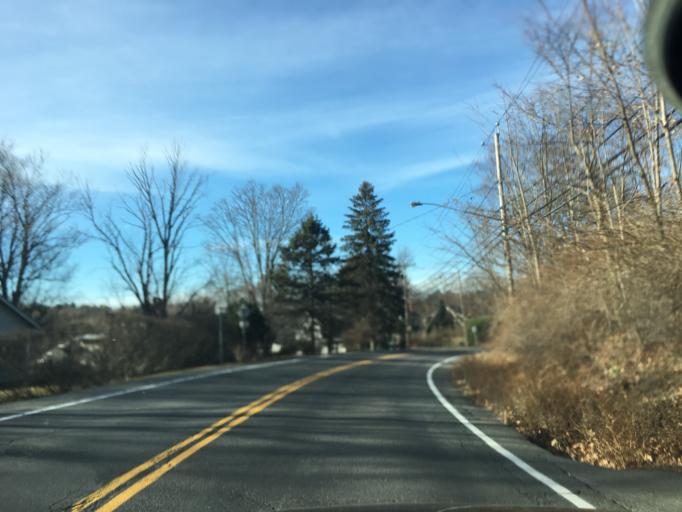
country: US
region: New York
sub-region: Rensselaer County
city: Averill Park
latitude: 42.6346
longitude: -73.5565
